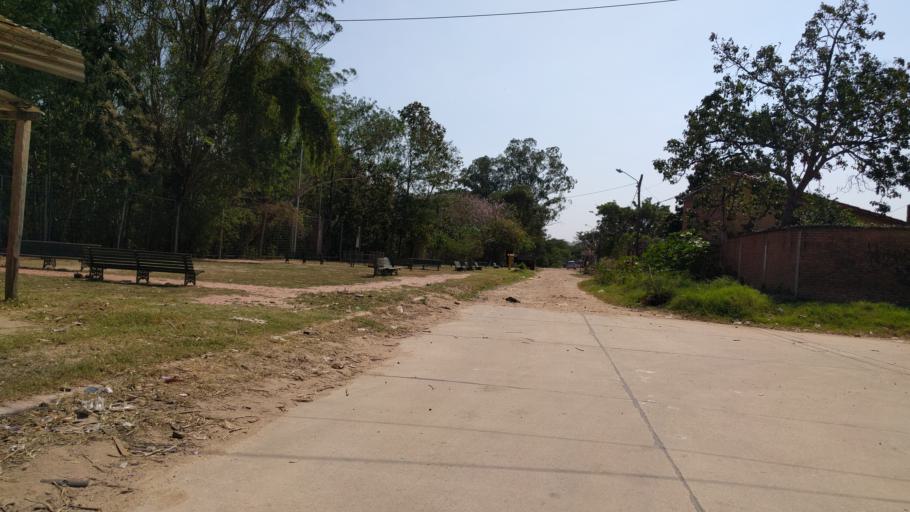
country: BO
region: Santa Cruz
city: Santa Cruz de la Sierra
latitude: -17.7991
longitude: -63.2247
